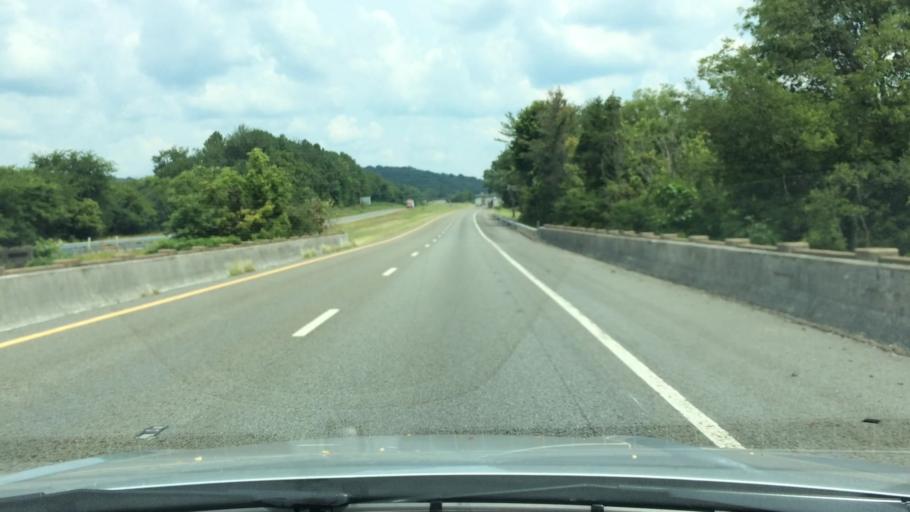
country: US
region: Tennessee
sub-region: Marshall County
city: Cornersville
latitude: 35.3176
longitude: -86.8820
